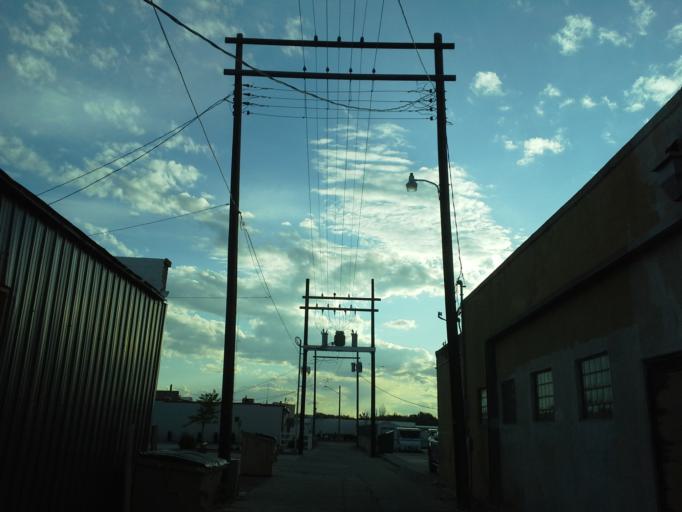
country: US
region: Wyoming
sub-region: Washakie County
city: Worland
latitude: 44.0174
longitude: -107.9601
